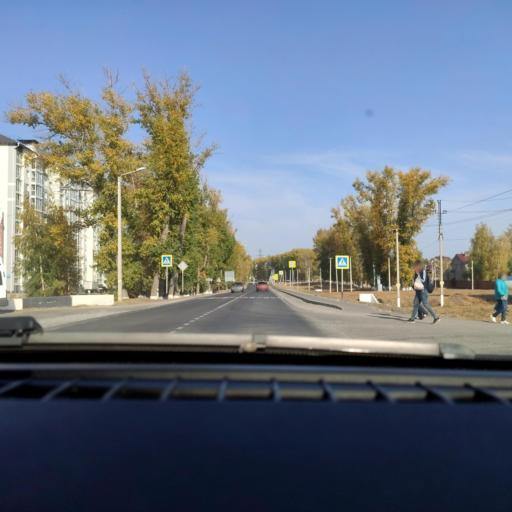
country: RU
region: Voronezj
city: Novaya Usman'
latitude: 51.6698
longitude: 39.4058
